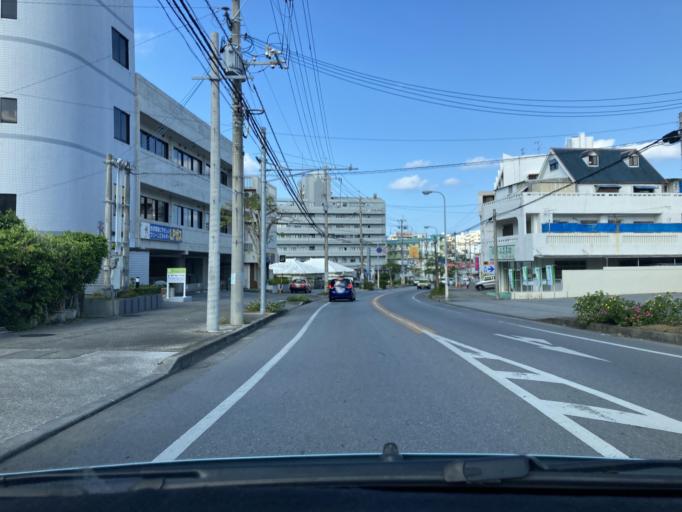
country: JP
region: Okinawa
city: Tomigusuku
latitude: 26.1925
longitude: 127.6779
